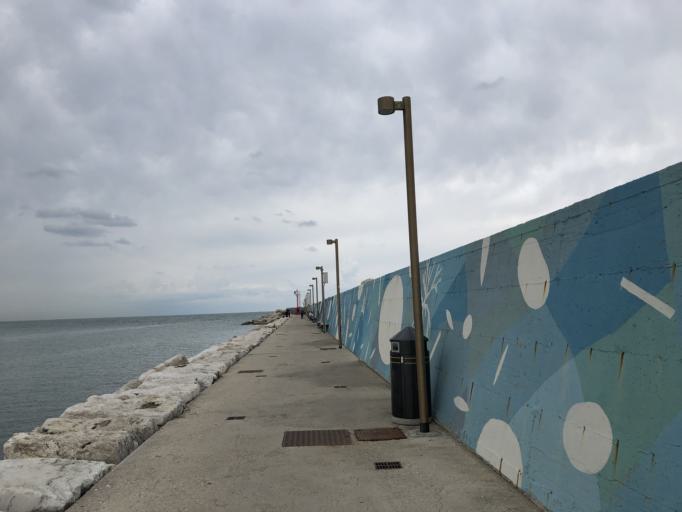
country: IT
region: The Marches
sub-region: Provincia di Pesaro e Urbino
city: Pesaro
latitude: 43.9264
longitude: 12.9069
